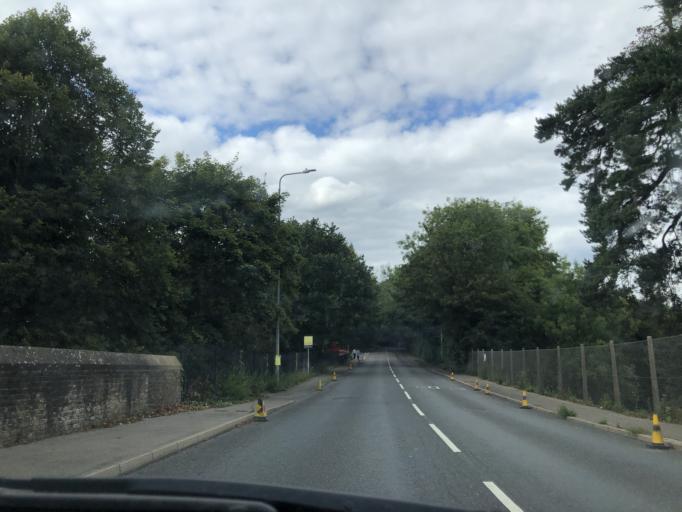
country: GB
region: England
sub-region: Kent
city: Sevenoaks
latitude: 51.2596
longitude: 0.1964
